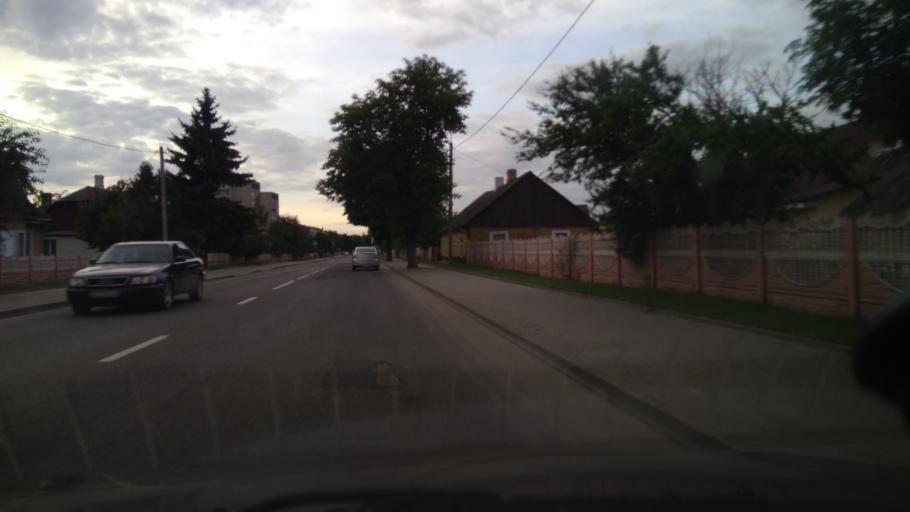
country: BY
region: Grodnenskaya
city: Shchuchin
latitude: 53.5990
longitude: 24.7431
